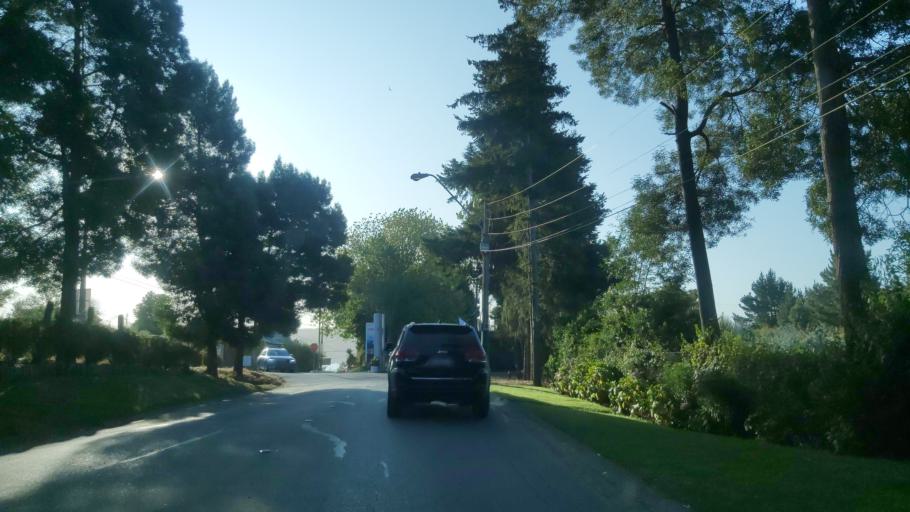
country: CL
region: Biobio
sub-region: Provincia de Concepcion
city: Tome
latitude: -36.5393
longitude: -72.9294
